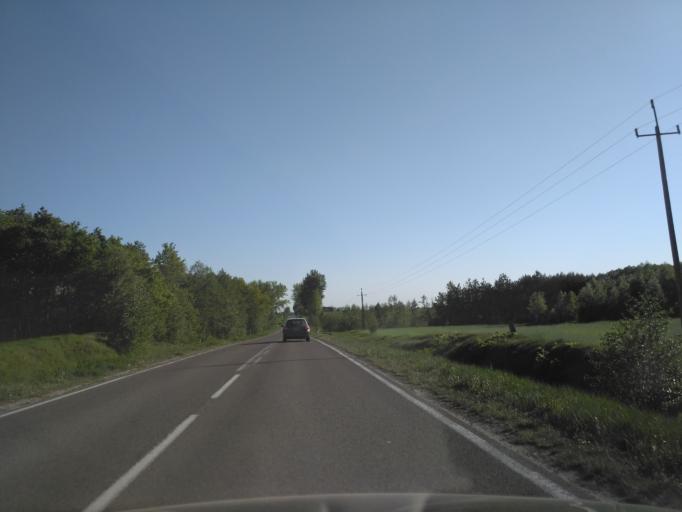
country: PL
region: Lublin Voivodeship
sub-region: Powiat swidnicki
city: Trawniki
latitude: 51.2126
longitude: 23.0721
